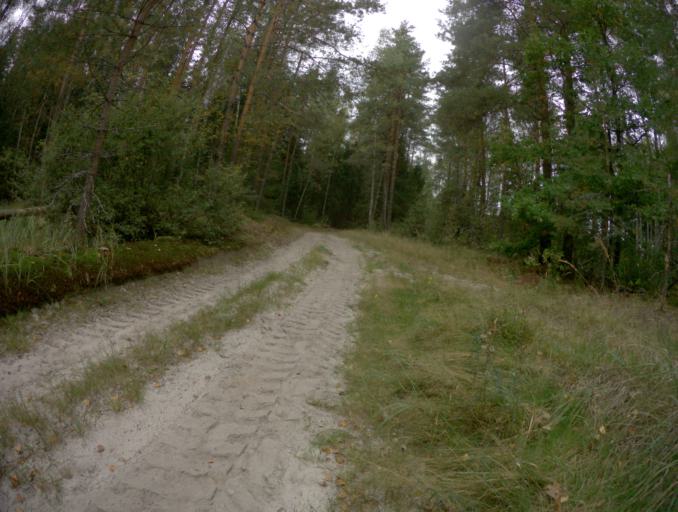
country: RU
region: Vladimir
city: Urshel'skiy
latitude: 55.8158
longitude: 40.2429
